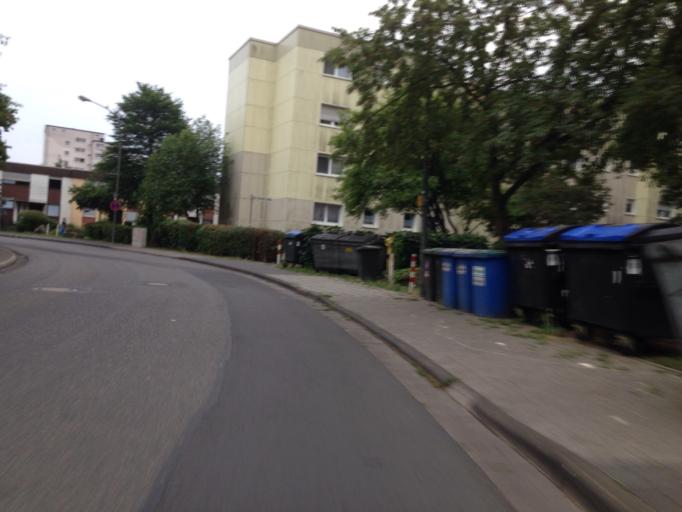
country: DE
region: Hesse
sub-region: Regierungsbezirk Giessen
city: Giessen
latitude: 50.5999
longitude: 8.6601
